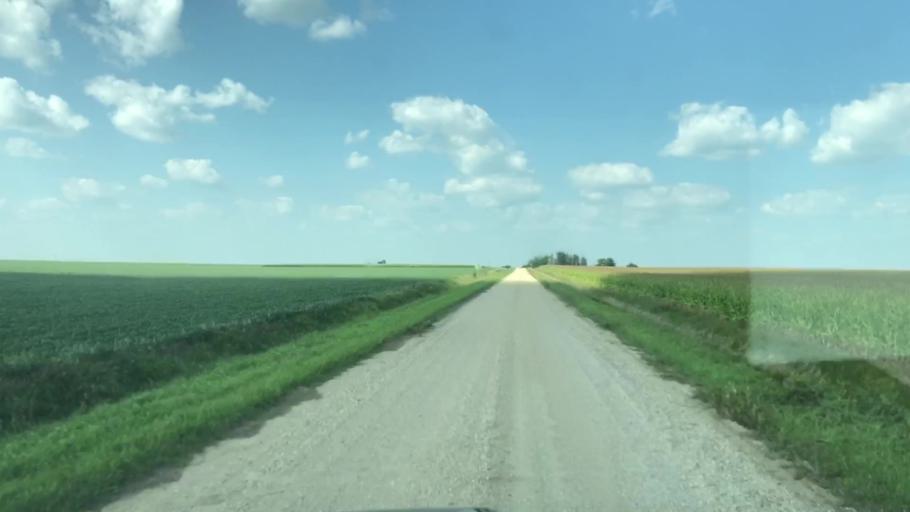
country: US
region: Iowa
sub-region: O'Brien County
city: Sheldon
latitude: 43.1793
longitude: -95.7824
